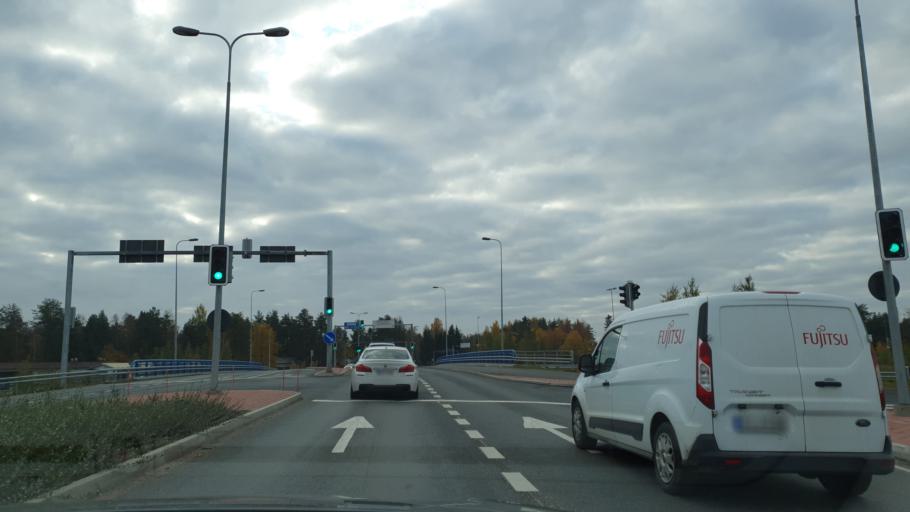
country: FI
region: Lapland
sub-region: Rovaniemi
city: Rovaniemi
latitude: 66.4909
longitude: 25.6923
